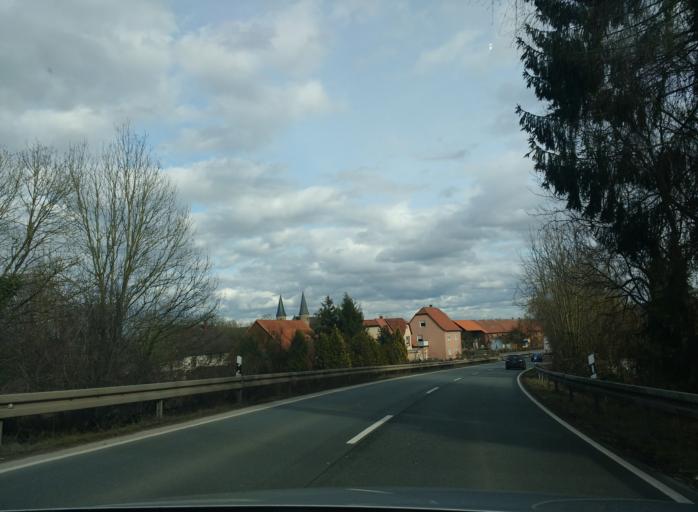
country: DE
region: Lower Saxony
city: Rinteln
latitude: 52.1667
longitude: 9.0297
